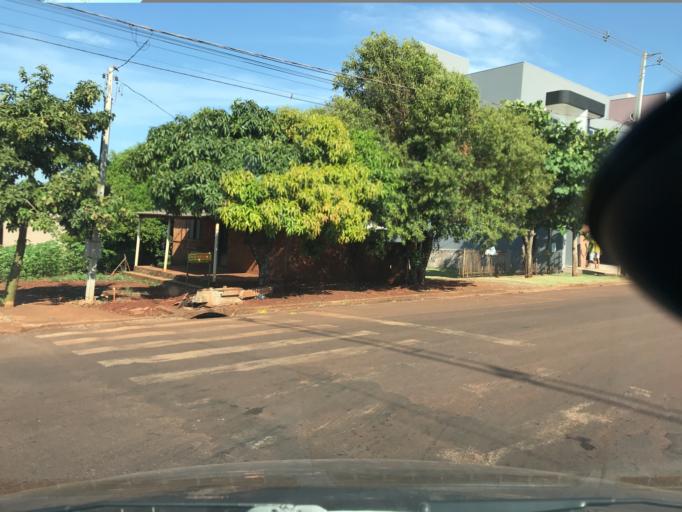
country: BR
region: Parana
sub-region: Palotina
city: Palotina
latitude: -24.2979
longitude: -53.8425
